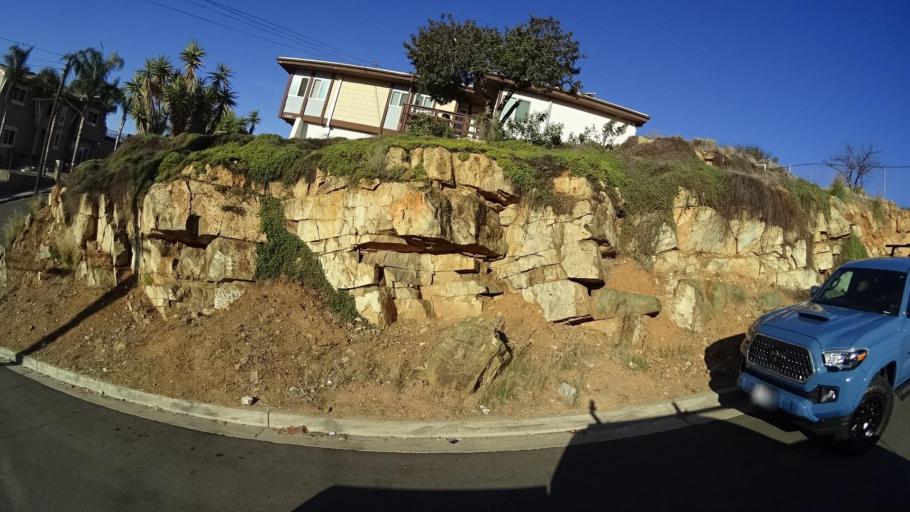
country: US
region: California
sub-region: San Diego County
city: La Presa
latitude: 32.7221
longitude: -116.9863
